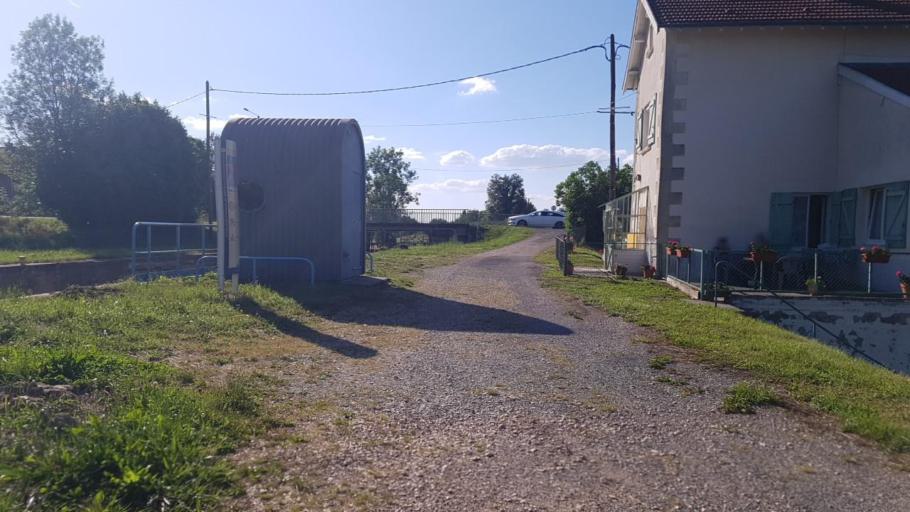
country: FR
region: Lorraine
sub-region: Departement de la Meuse
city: Revigny-sur-Ornain
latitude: 48.8157
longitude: 5.0432
